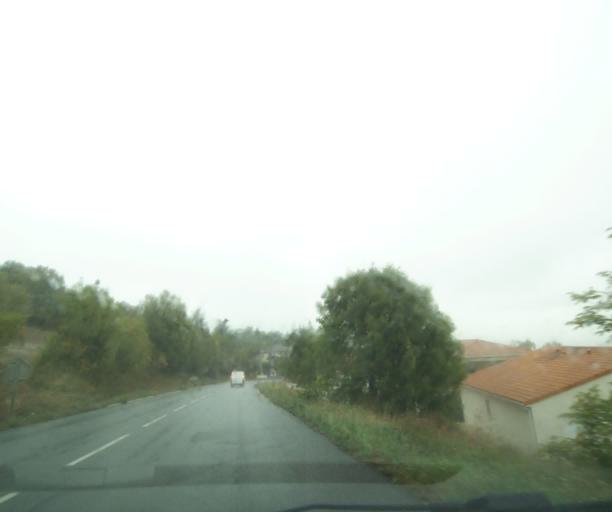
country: FR
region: Auvergne
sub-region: Departement du Puy-de-Dome
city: Chateaugay
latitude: 45.8467
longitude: 3.0899
